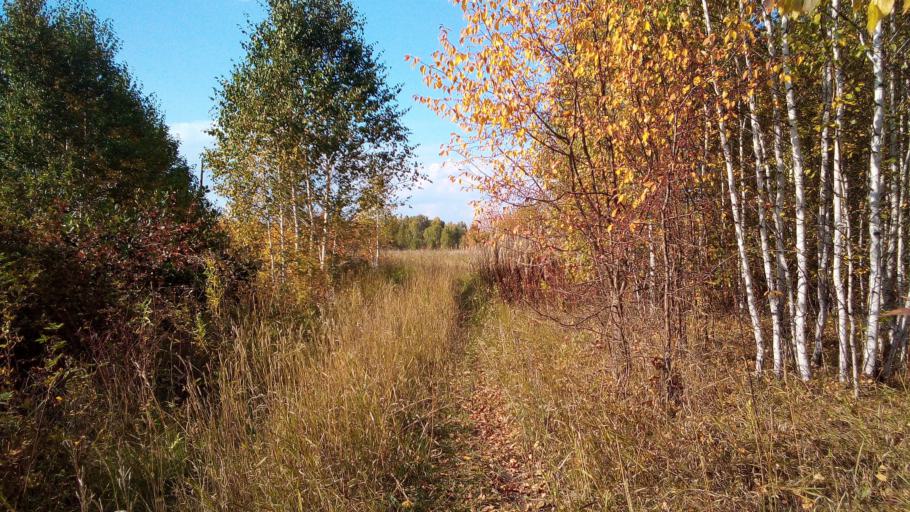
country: RU
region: Chelyabinsk
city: Timiryazevskiy
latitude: 54.9952
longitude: 60.8502
